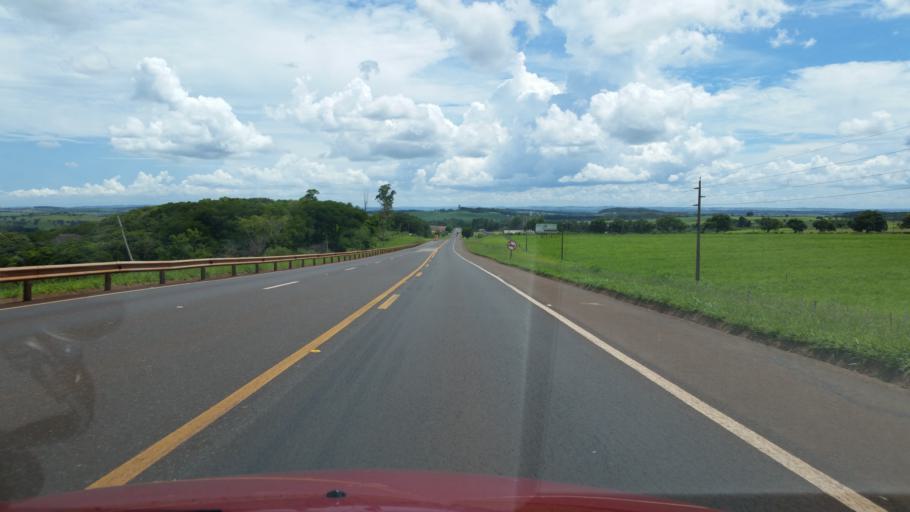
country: BR
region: Sao Paulo
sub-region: Avare
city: Avare
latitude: -23.1415
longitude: -48.9430
